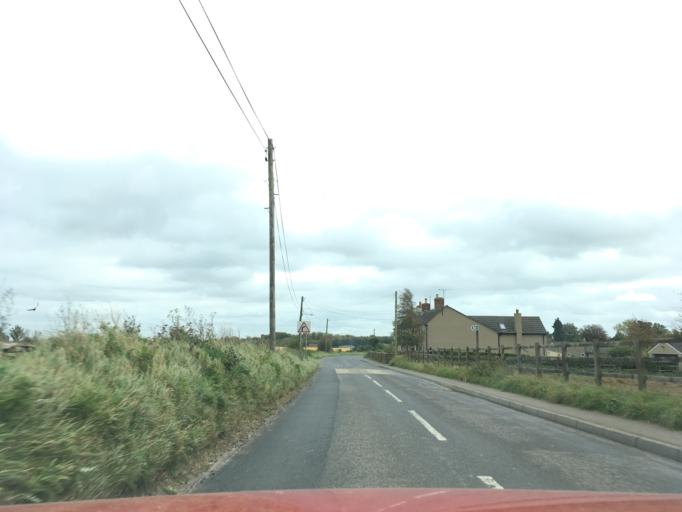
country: GB
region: England
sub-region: South Gloucestershire
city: Horton
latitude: 51.5783
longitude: -2.3141
